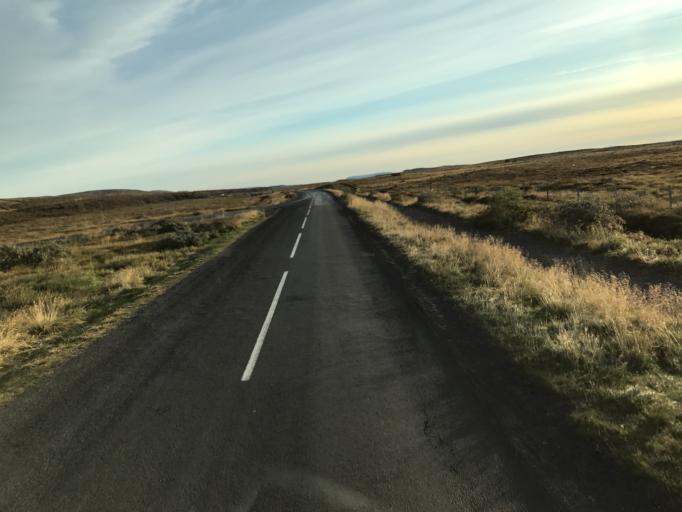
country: IS
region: South
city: Vestmannaeyjar
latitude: 64.3256
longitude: -20.1316
